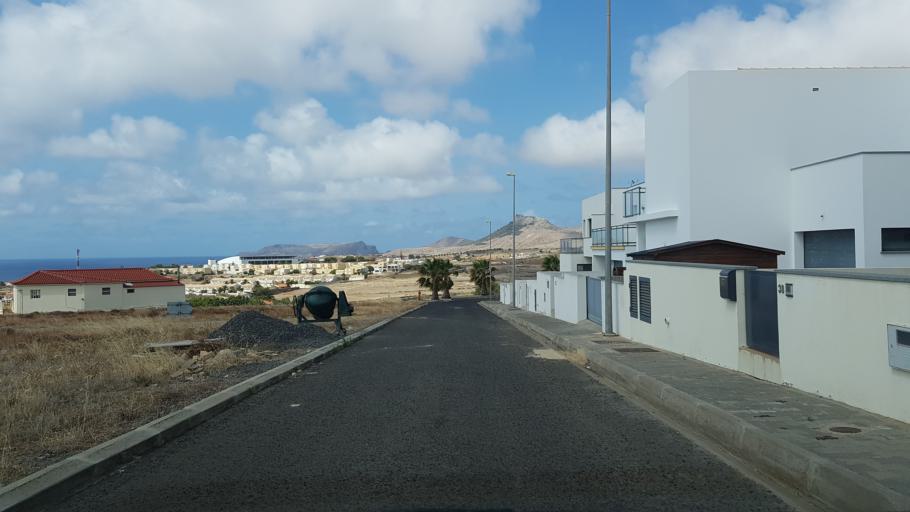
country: PT
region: Madeira
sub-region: Porto Santo
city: Vila de Porto Santo
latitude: 33.0682
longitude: -16.3337
